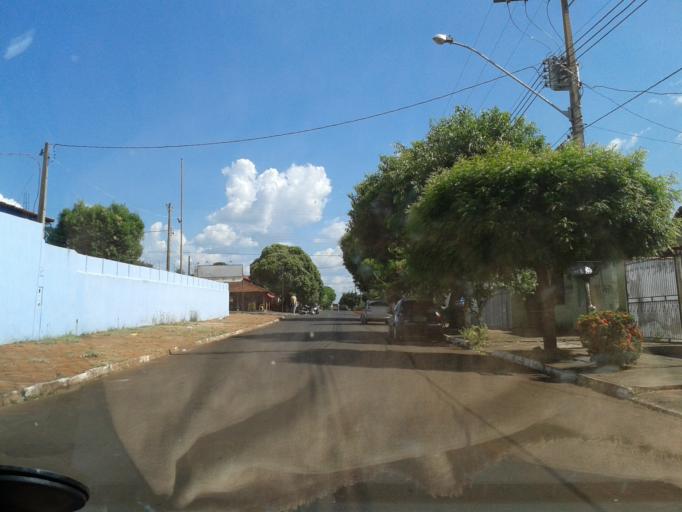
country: BR
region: Minas Gerais
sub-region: Ituiutaba
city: Ituiutaba
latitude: -18.9878
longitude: -49.4690
